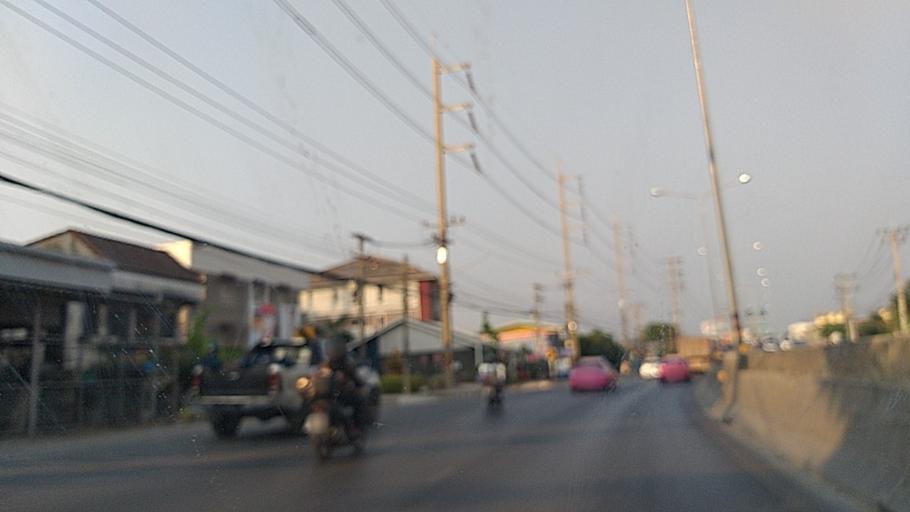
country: TH
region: Phra Nakhon Si Ayutthaya
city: Ban Bang Kadi Pathum Thani
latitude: 13.9940
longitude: 100.5512
